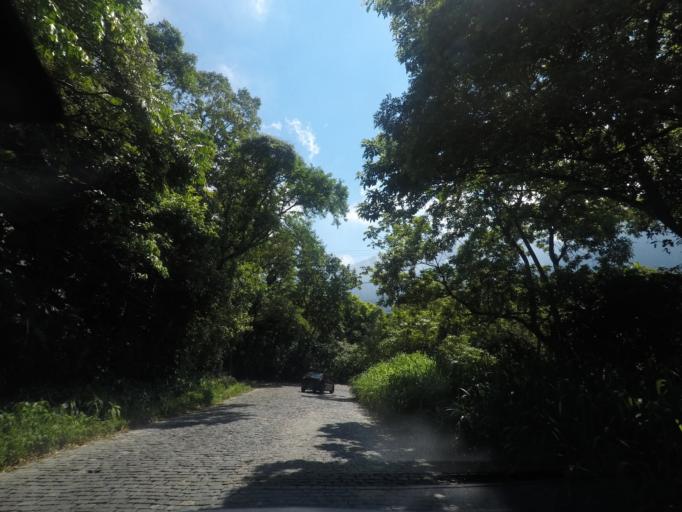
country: BR
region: Rio de Janeiro
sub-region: Petropolis
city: Petropolis
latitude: -22.5443
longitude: -43.1804
